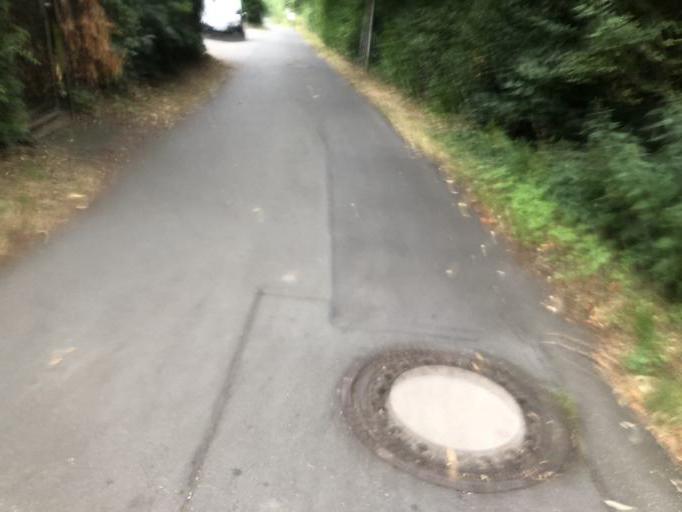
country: DE
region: Bavaria
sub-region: Regierungsbezirk Mittelfranken
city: Furth
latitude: 49.4970
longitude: 10.9816
